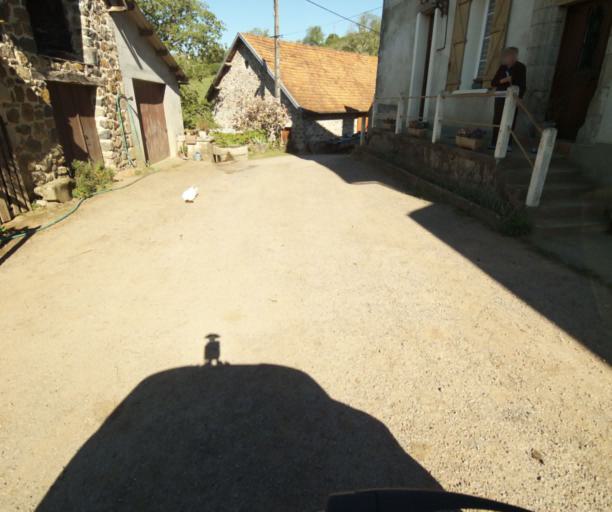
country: FR
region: Limousin
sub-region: Departement de la Correze
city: Tulle
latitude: 45.2819
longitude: 1.7800
